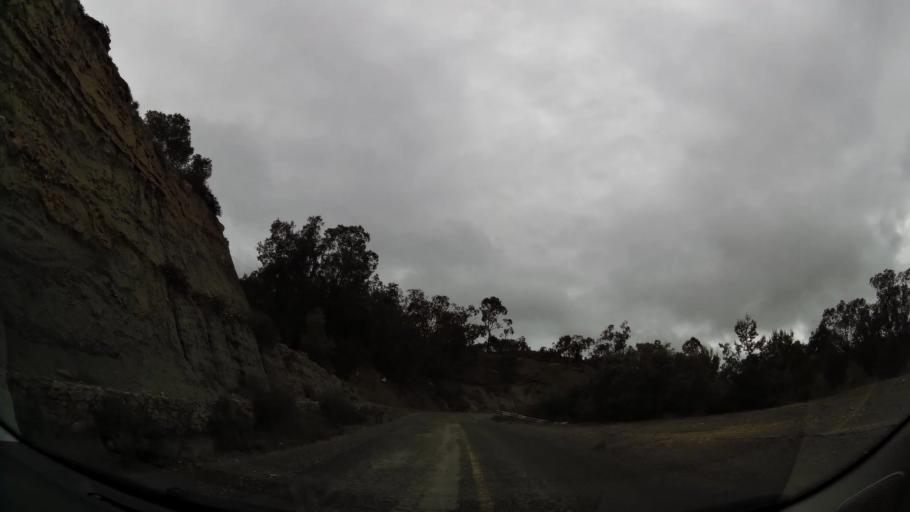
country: MA
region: Taza-Al Hoceima-Taounate
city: Imzourene
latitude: 34.9480
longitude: -3.8060
